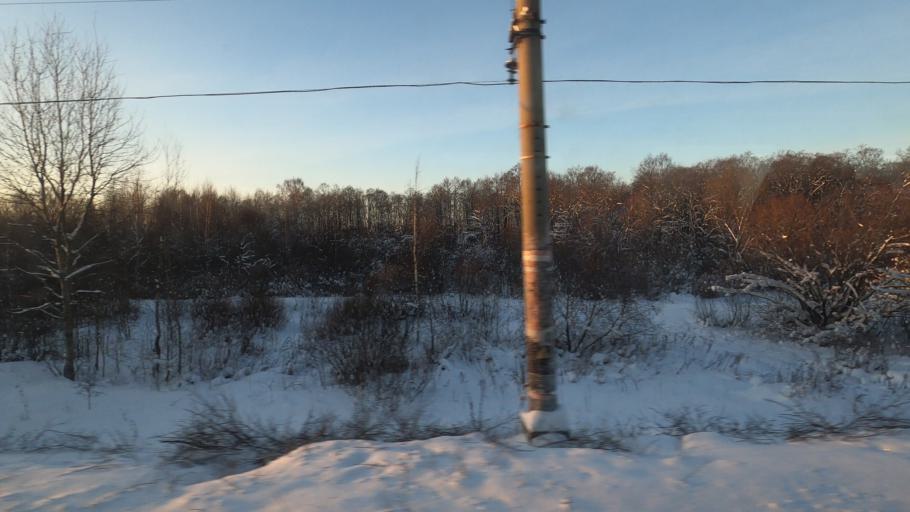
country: RU
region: Moskovskaya
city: Orud'yevo
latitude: 56.4408
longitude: 37.5123
